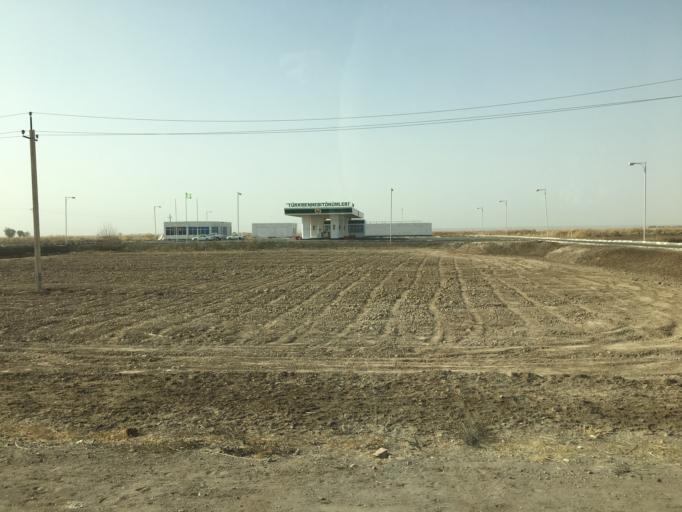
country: TM
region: Dasoguz
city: Koeneuergench
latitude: 41.7366
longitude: 58.6863
